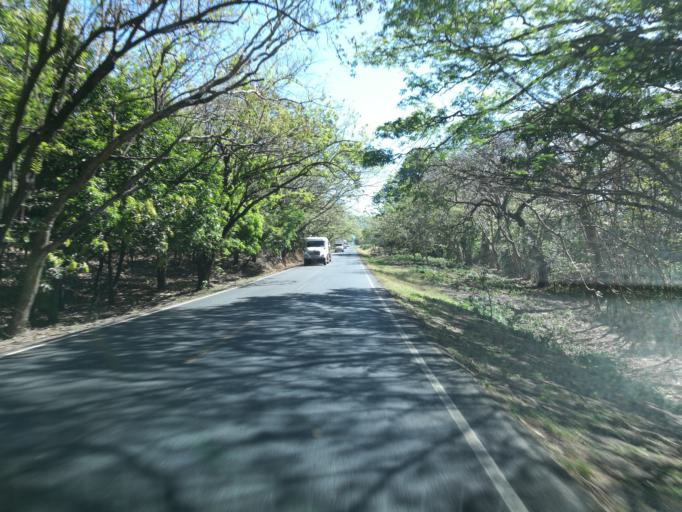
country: CR
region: Puntarenas
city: Miramar
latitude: 10.0913
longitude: -84.8269
